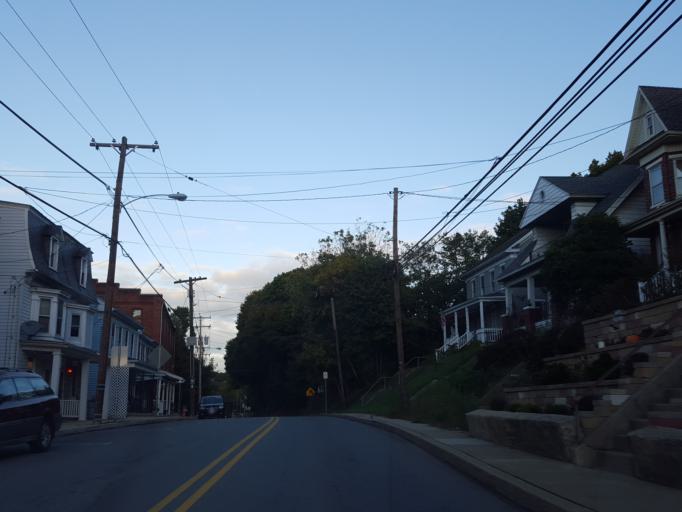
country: US
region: Pennsylvania
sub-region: York County
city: Windsor
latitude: 39.9149
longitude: -76.5797
